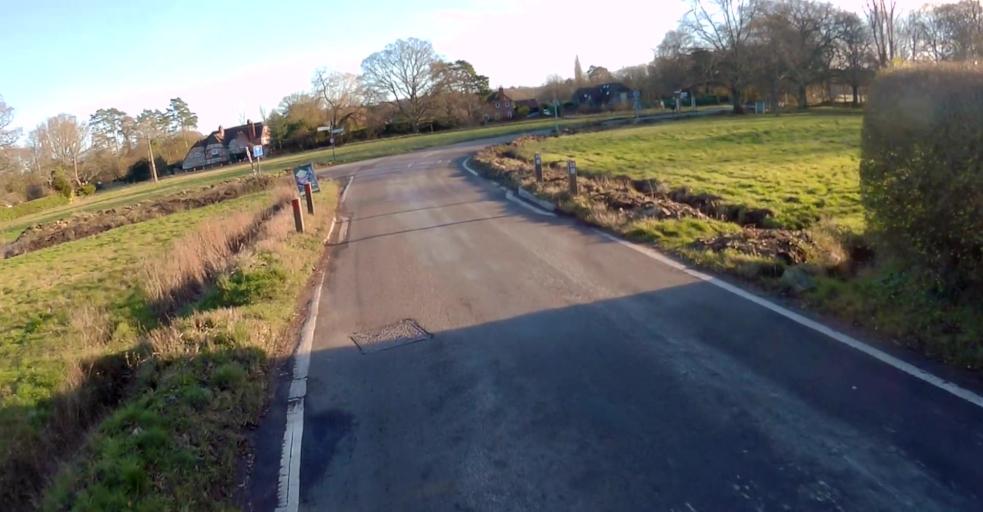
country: GB
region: England
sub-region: Hampshire
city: Hook
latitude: 51.2815
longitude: -0.9902
